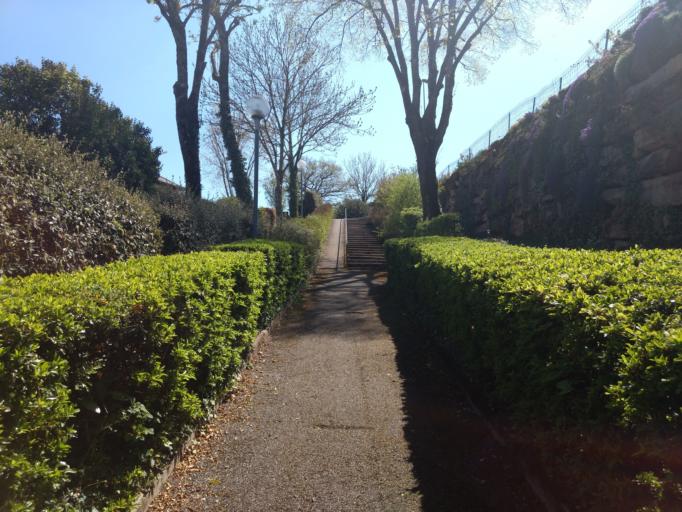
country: FR
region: Midi-Pyrenees
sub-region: Departement de l'Aveyron
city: Olemps
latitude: 44.3626
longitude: 2.5525
